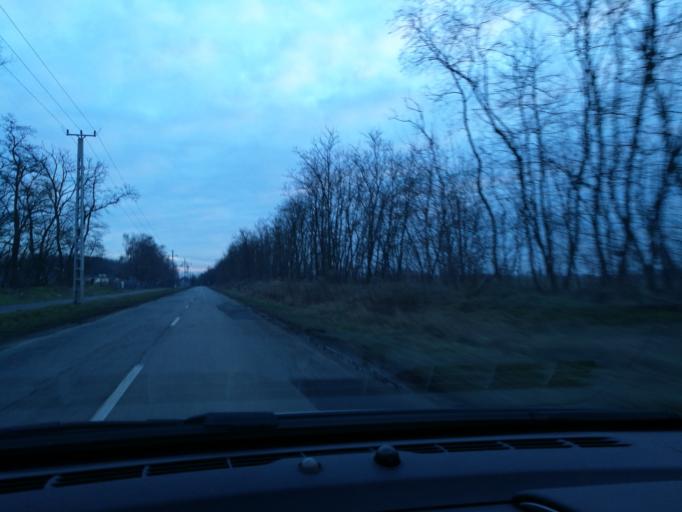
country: HU
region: Szabolcs-Szatmar-Bereg
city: Nyiregyhaza
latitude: 47.9825
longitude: 21.7046
